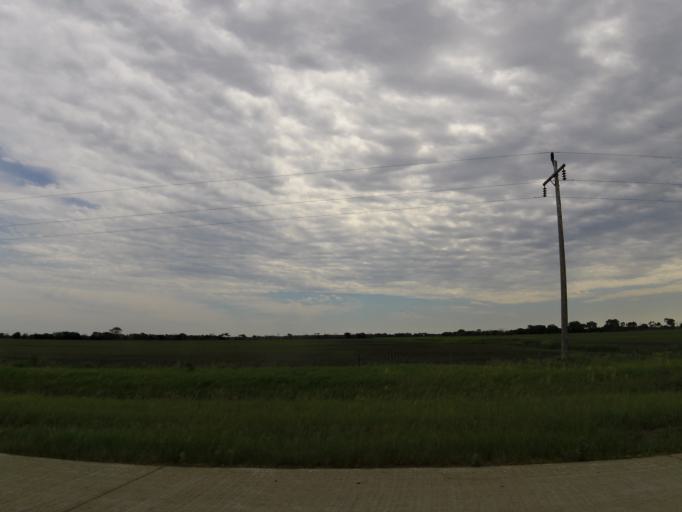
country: US
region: North Dakota
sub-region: Walsh County
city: Grafton
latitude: 48.3977
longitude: -97.1901
